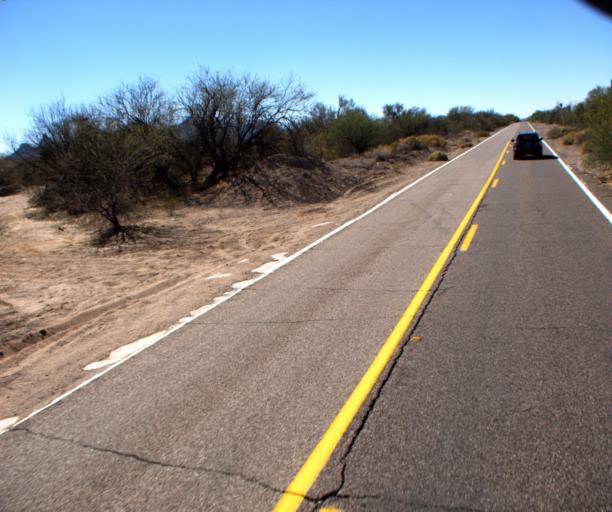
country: US
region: Arizona
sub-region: Pima County
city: Ajo
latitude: 32.1780
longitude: -112.7621
